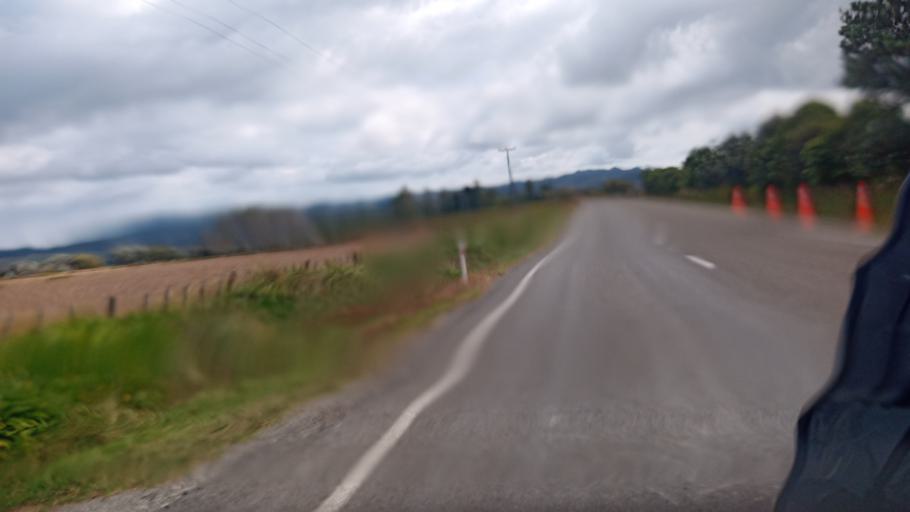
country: NZ
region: Gisborne
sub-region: Gisborne District
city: Gisborne
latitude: -38.3449
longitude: 178.2976
